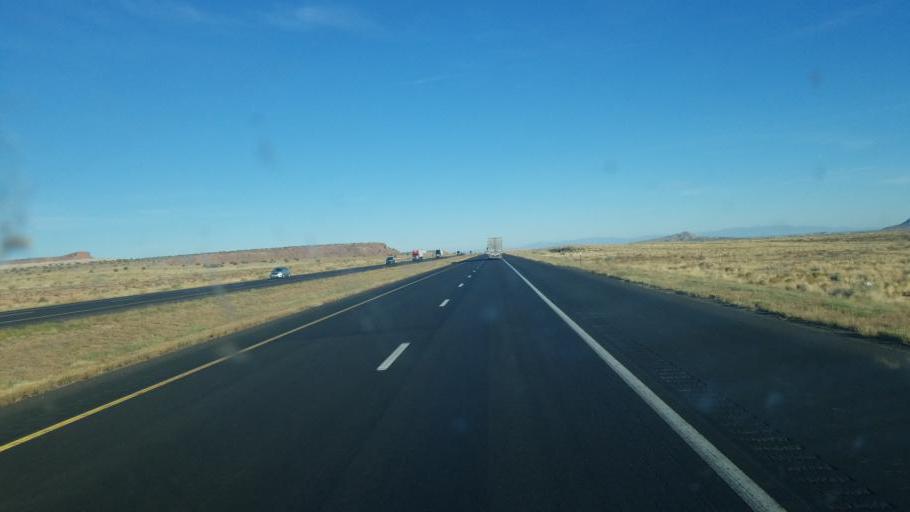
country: US
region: New Mexico
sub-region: Cibola County
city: Laguna
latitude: 34.9920
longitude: -107.2288
